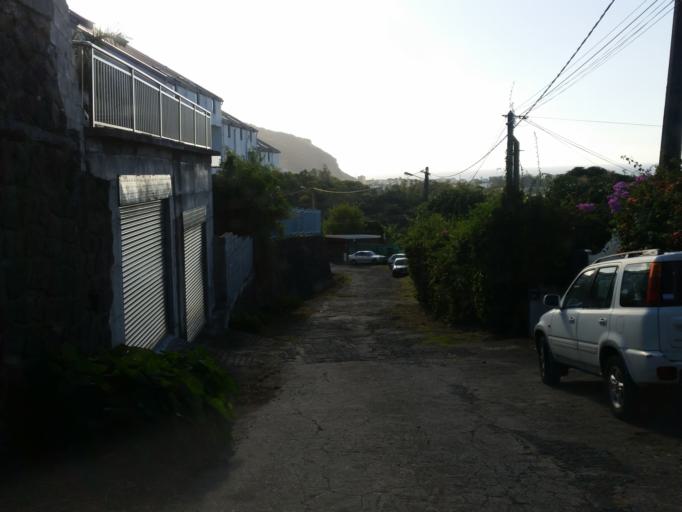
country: RE
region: Reunion
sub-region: Reunion
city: Saint-Denis
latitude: -20.9000
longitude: 55.4577
